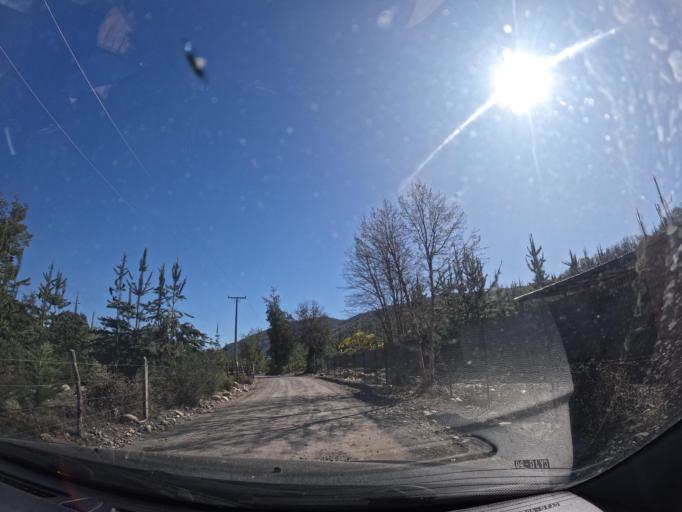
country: CL
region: Maule
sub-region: Provincia de Linares
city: Longavi
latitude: -36.2314
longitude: -71.3703
